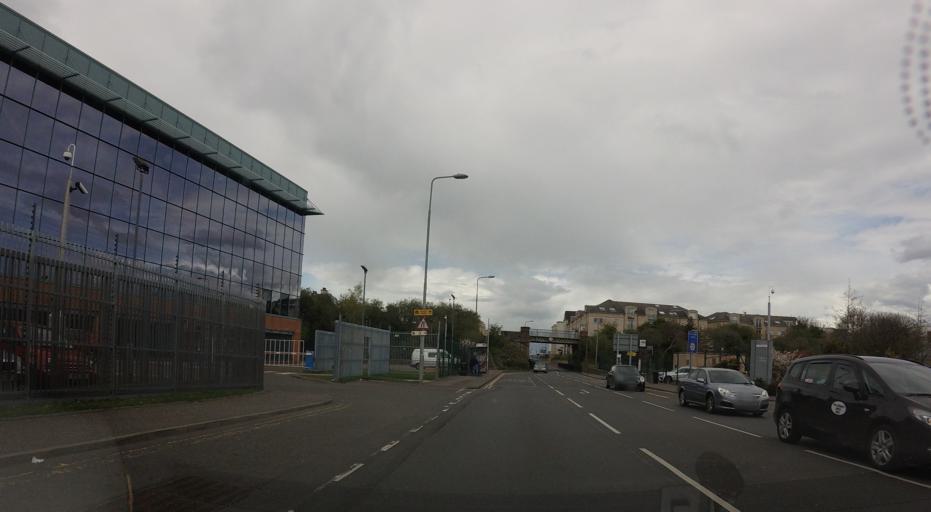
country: GB
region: Scotland
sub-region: Edinburgh
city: Edinburgh
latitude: 55.9692
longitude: -3.2365
